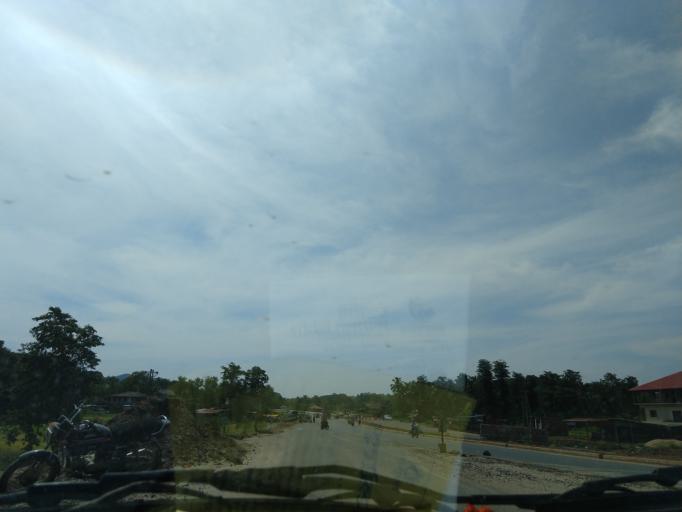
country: IN
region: Maharashtra
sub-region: Sindhudurg
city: Kudal
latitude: 15.9525
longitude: 73.7388
